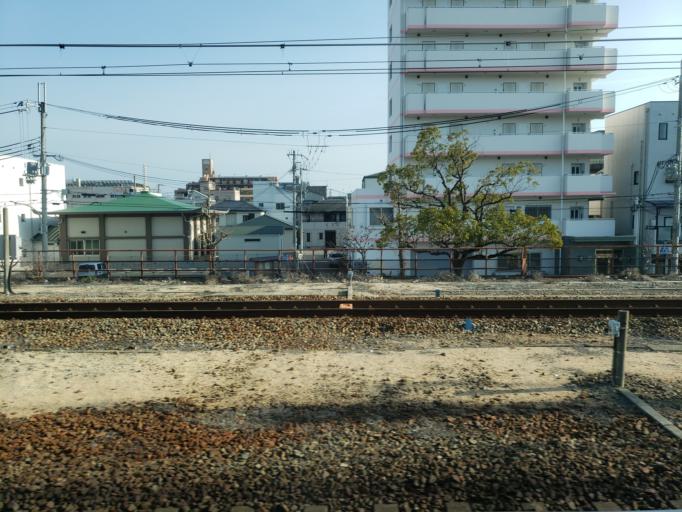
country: JP
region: Hyogo
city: Kobe
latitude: 34.6506
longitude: 135.1335
